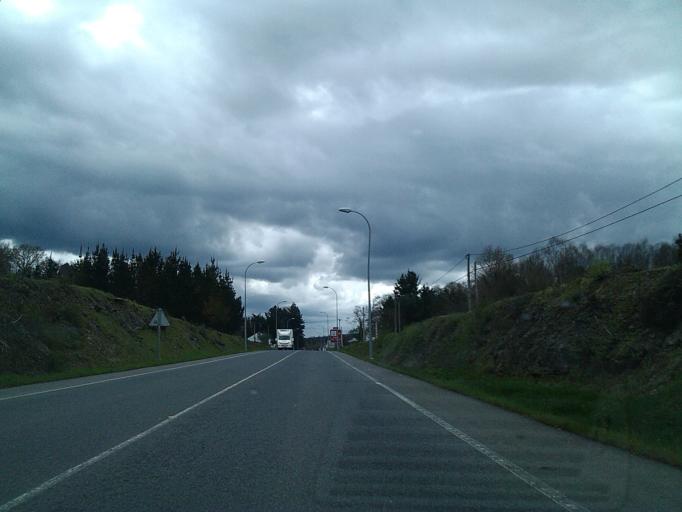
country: ES
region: Galicia
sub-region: Provincia de Lugo
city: Guitiriz
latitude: 43.1821
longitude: -7.8266
